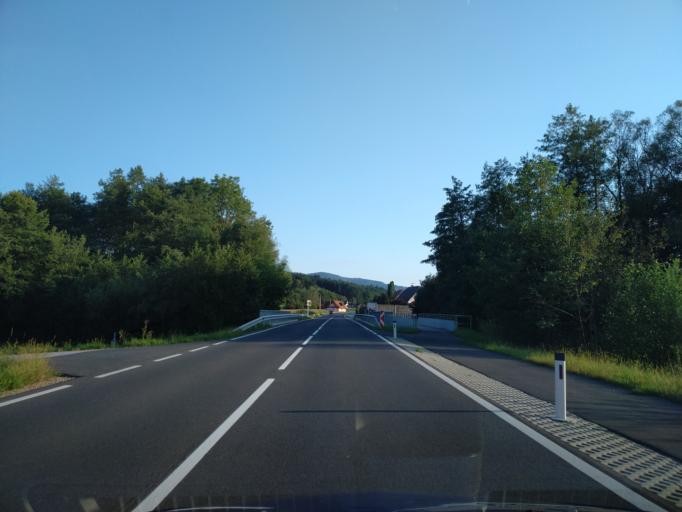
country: AT
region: Styria
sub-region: Politischer Bezirk Deutschlandsberg
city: Wies
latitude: 46.7153
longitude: 15.2530
